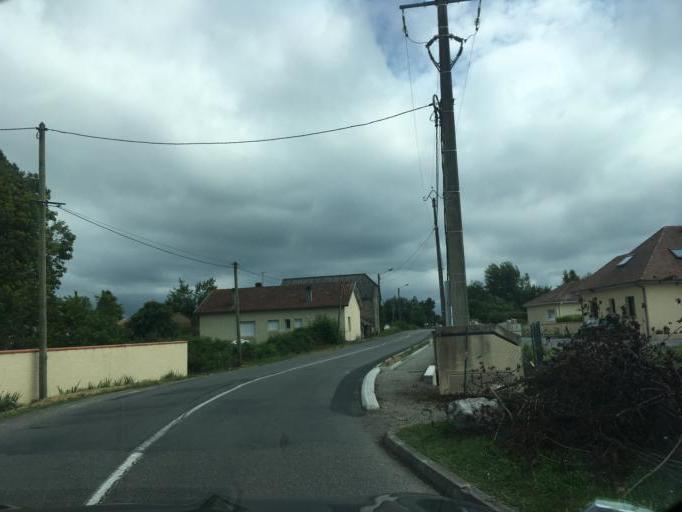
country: FR
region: Aquitaine
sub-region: Departement des Pyrenees-Atlantiques
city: Ousse
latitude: 43.2951
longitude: -0.2723
